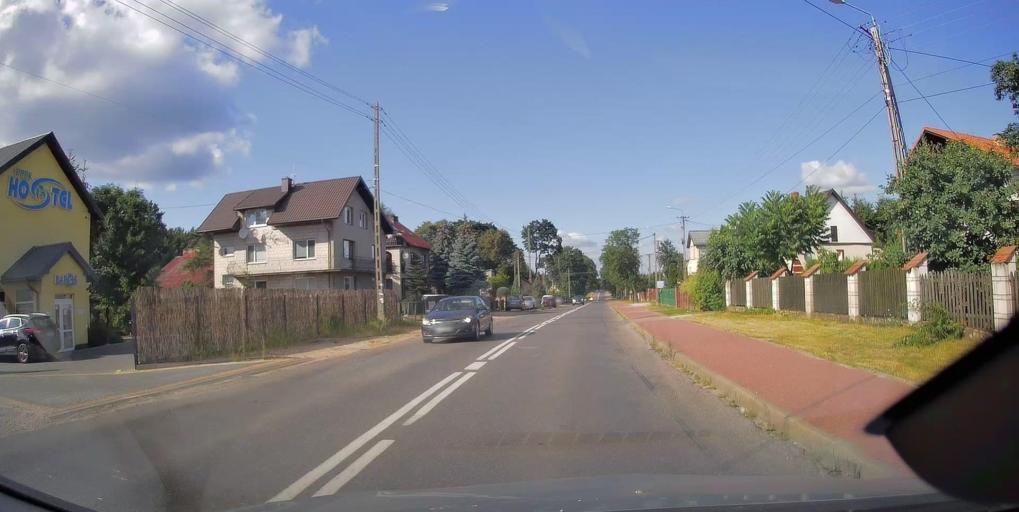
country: PL
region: Swietokrzyskie
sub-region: Powiat skarzyski
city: Suchedniow
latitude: 51.0264
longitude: 20.8365
